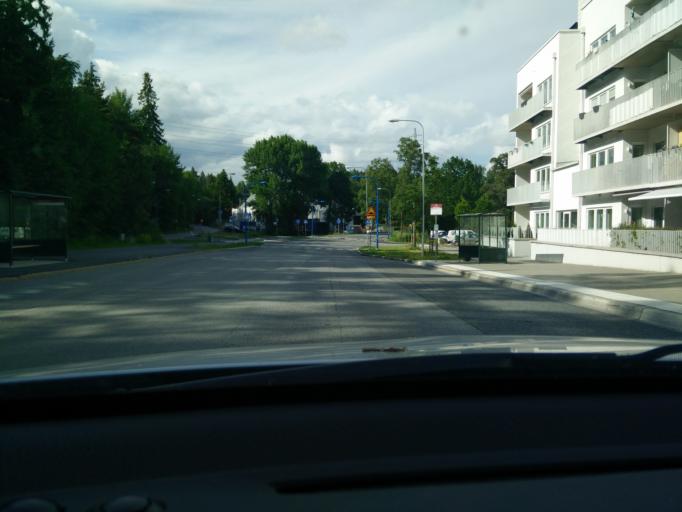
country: SE
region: Stockholm
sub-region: Sollentuna Kommun
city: Sollentuna
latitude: 59.4483
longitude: 17.9510
